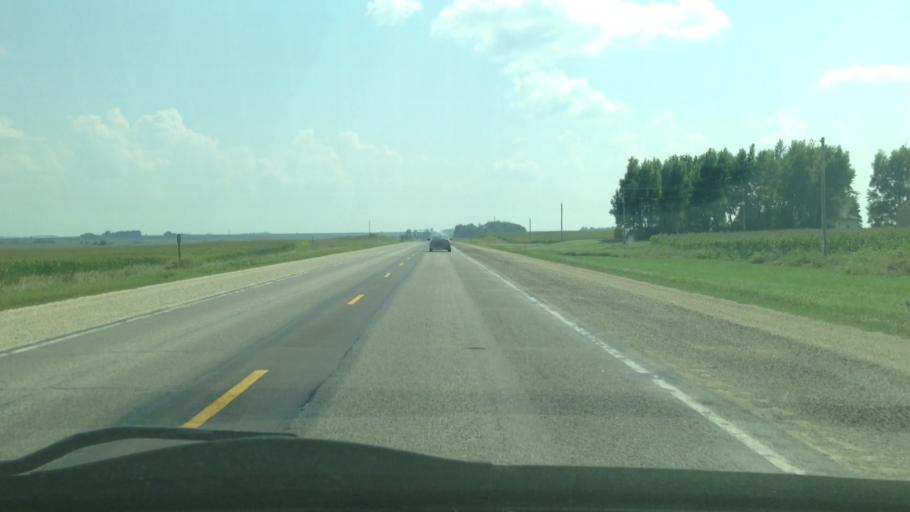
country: US
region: Iowa
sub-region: Howard County
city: Cresco
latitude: 43.3538
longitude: -92.2985
